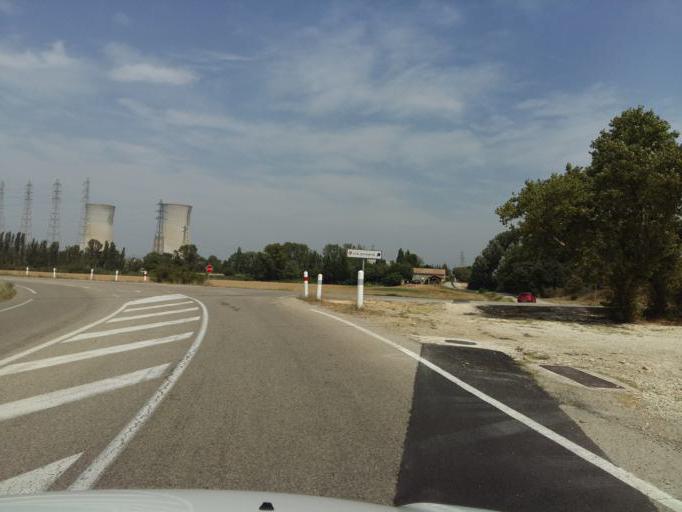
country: FR
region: Provence-Alpes-Cote d'Azur
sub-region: Departement du Vaucluse
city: Bollene
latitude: 44.3186
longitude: 4.7348
